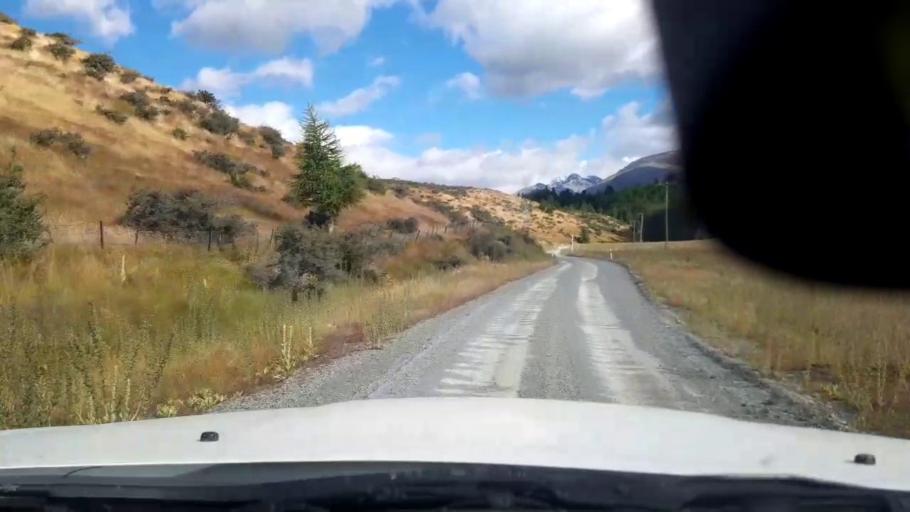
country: NZ
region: Canterbury
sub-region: Timaru District
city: Pleasant Point
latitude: -43.8774
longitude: 170.4655
